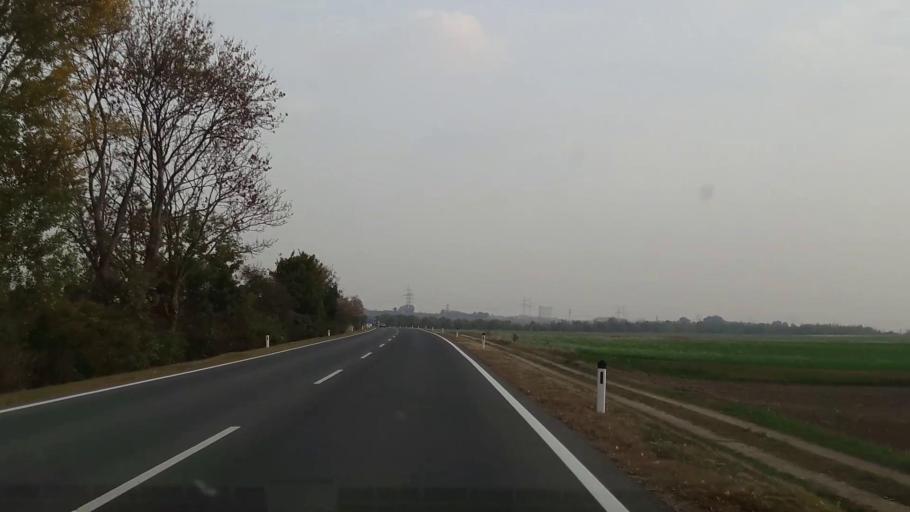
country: AT
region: Burgenland
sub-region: Politischer Bezirk Neusiedl am See
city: Parndorf
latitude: 48.0085
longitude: 16.8243
